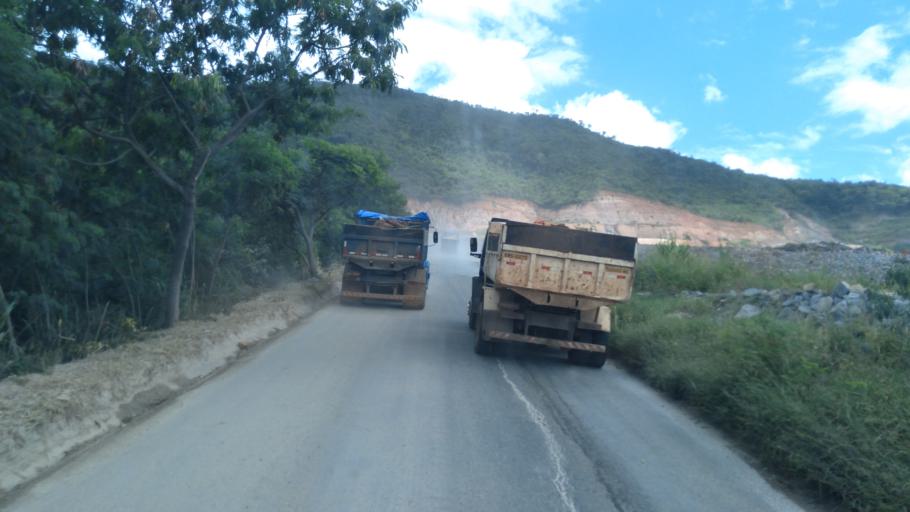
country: BR
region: Minas Gerais
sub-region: Santa Luzia
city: Santa Luzia
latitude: -19.8539
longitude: -43.8498
